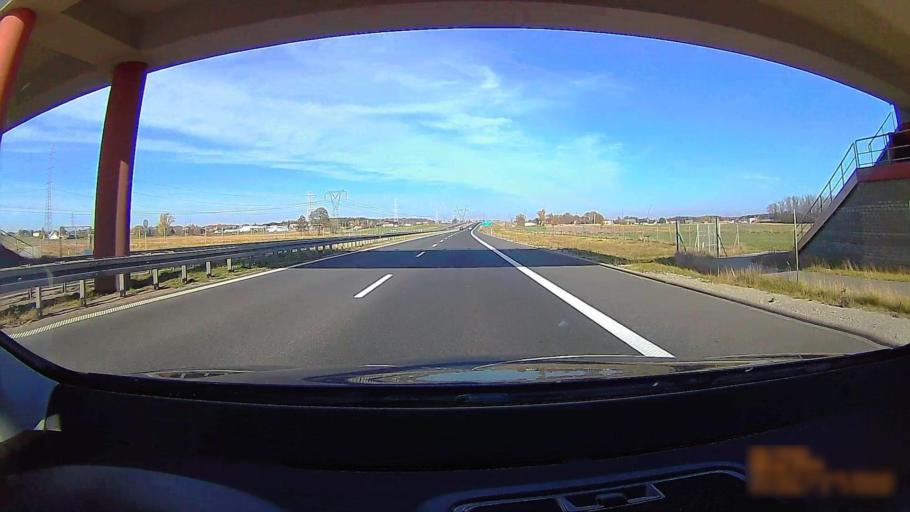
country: PL
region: Greater Poland Voivodeship
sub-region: Powiat ostrowski
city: Przygodzice
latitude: 51.5992
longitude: 17.8518
